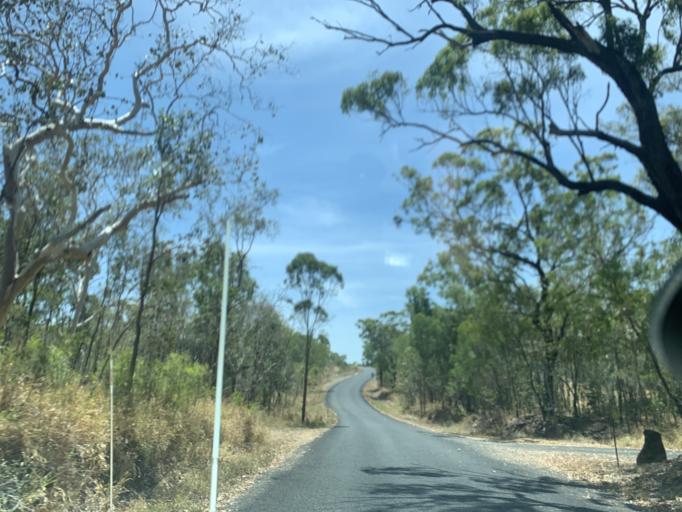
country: AU
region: Queensland
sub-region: Tablelands
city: Kuranda
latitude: -16.9080
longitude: 145.5685
